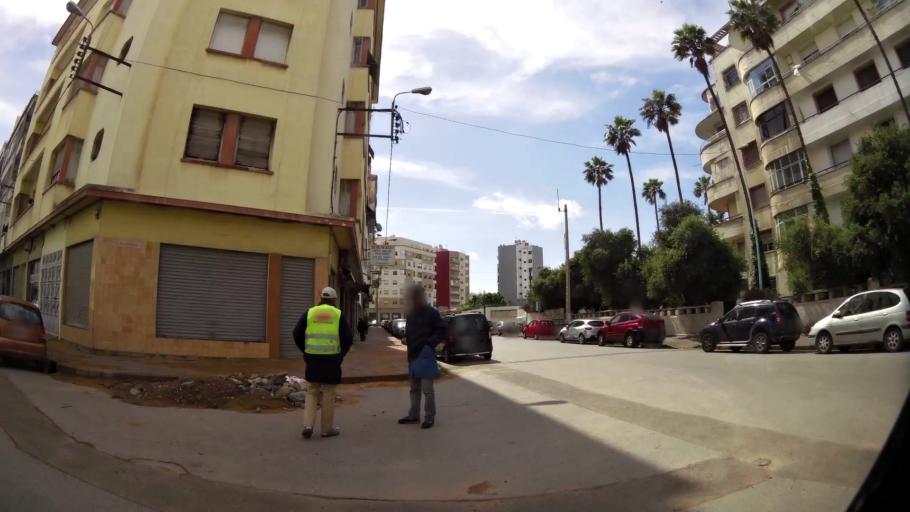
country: MA
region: Grand Casablanca
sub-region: Casablanca
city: Casablanca
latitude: 33.5917
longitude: -7.5992
